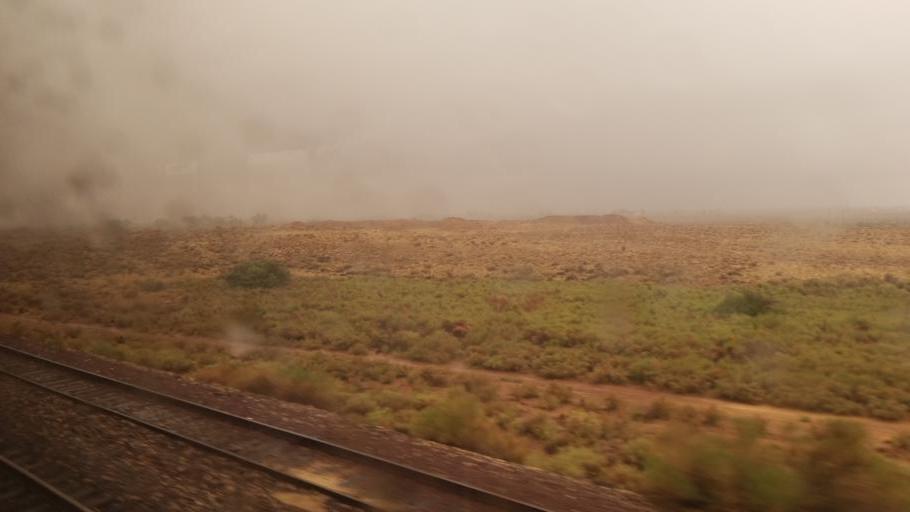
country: US
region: Arizona
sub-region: Navajo County
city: Joseph City
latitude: 34.9069
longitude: -110.2582
